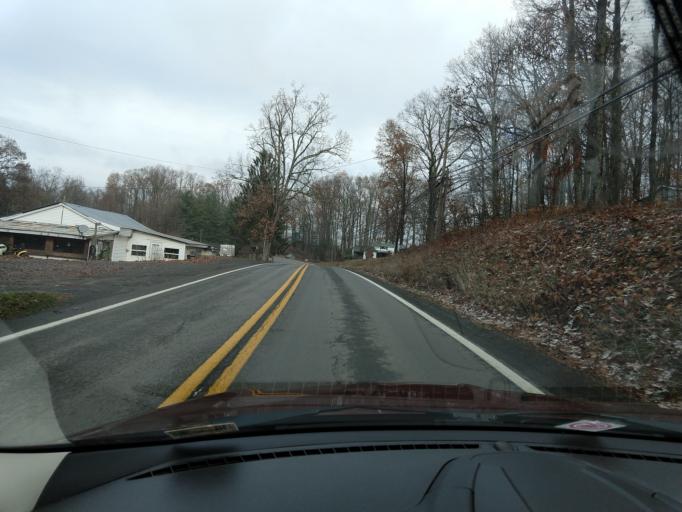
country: US
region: West Virginia
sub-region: Nicholas County
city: Craigsville
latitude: 38.1900
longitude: -80.6852
